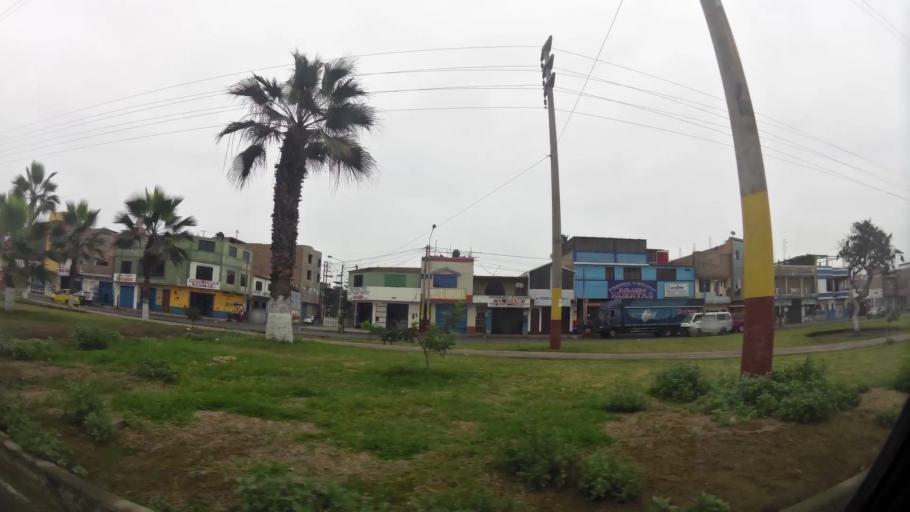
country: PE
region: Ancash
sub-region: Provincia de Santa
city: Chimbote
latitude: -9.0803
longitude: -78.5781
